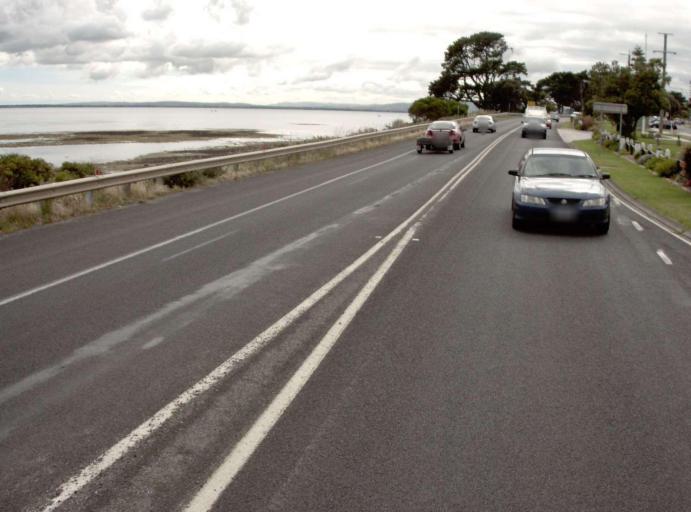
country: AU
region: Victoria
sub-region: Bass Coast
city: Phillip Island
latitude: -38.5207
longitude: 145.3699
